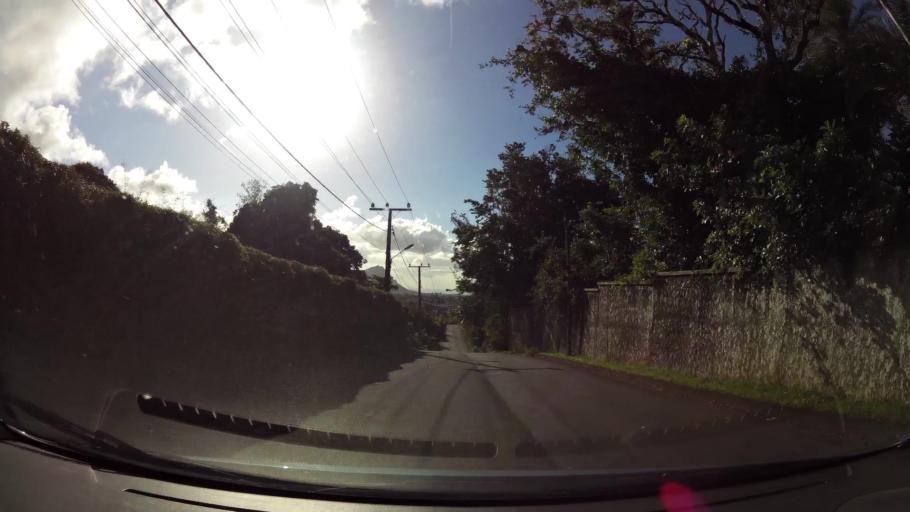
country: MU
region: Plaines Wilhems
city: Curepipe
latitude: -20.3139
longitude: 57.4981
